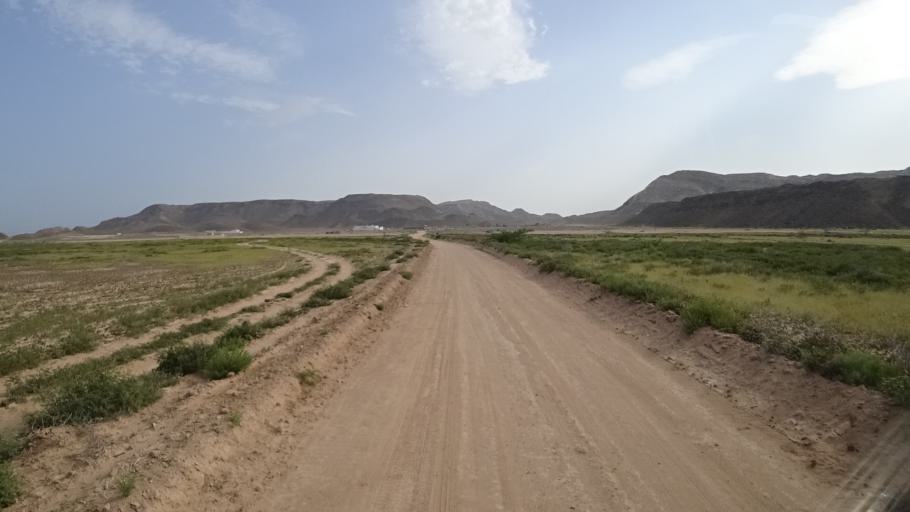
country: OM
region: Ash Sharqiyah
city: Sur
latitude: 22.4433
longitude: 59.8225
